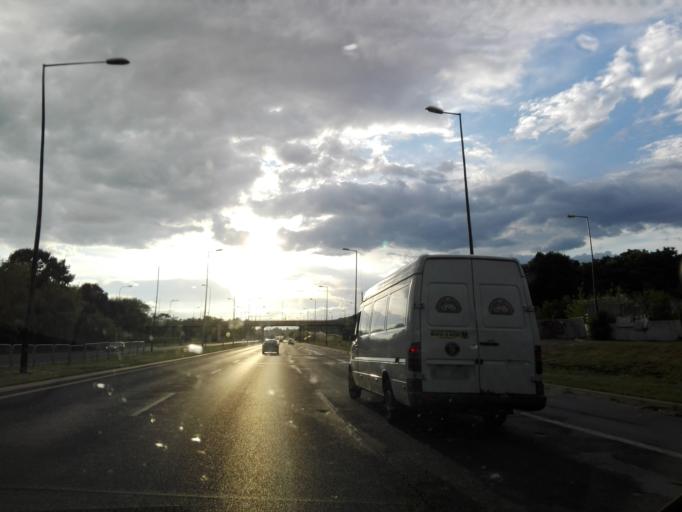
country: PL
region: Lublin Voivodeship
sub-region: Powiat lubelski
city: Lublin
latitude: 51.2538
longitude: 22.5474
